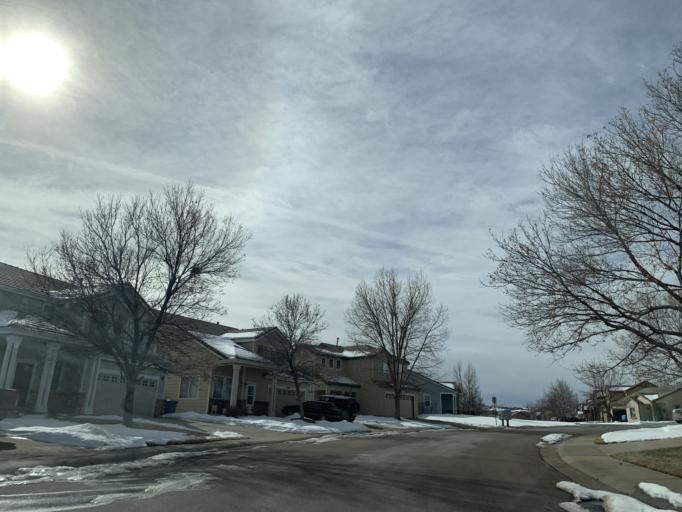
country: US
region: Colorado
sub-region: Douglas County
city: Carriage Club
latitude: 39.5288
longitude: -104.9312
